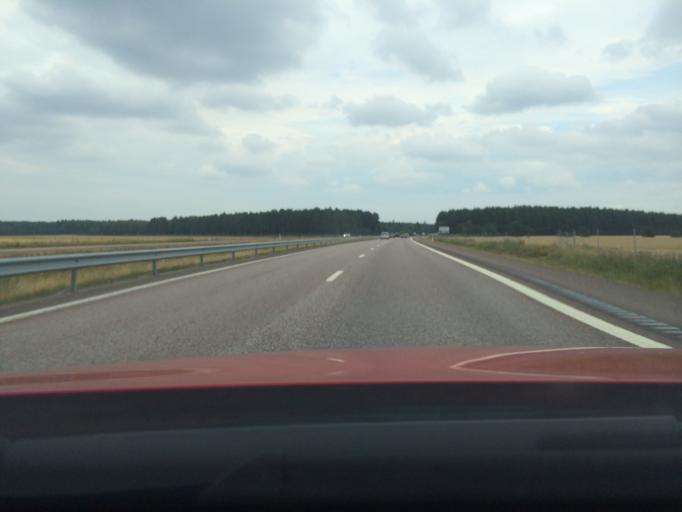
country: SE
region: Soedermanland
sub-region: Nykopings Kommun
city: Stigtomta
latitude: 58.7557
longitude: 16.7732
